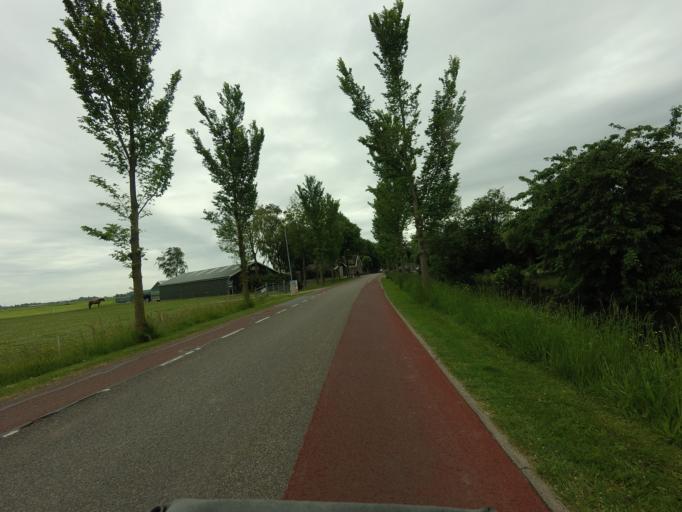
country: NL
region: North Holland
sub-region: Gemeente Medemblik
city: Opperdoes
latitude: 52.7149
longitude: 5.0760
